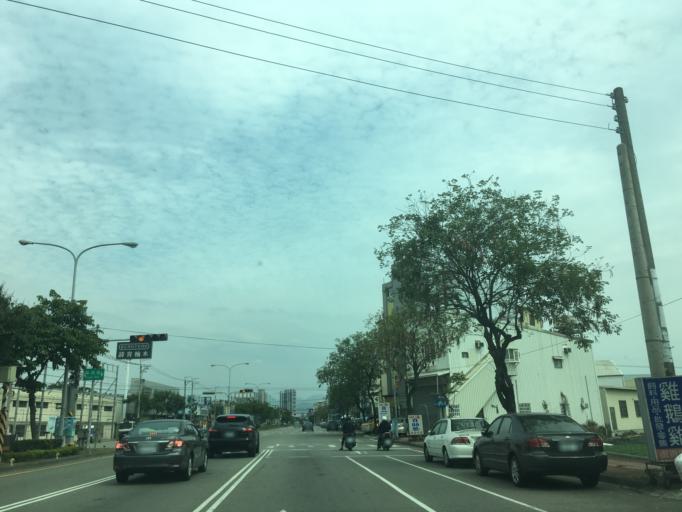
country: TW
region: Taiwan
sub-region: Taichung City
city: Taichung
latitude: 24.1065
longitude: 120.6653
